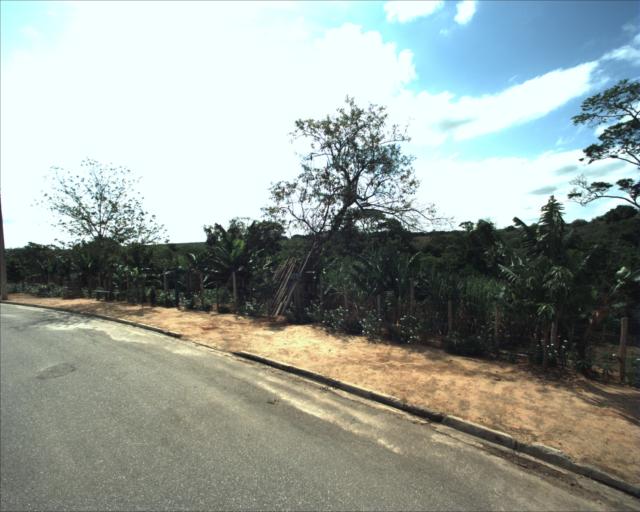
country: BR
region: Sao Paulo
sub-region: Sorocaba
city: Sorocaba
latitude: -23.3899
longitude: -47.3787
